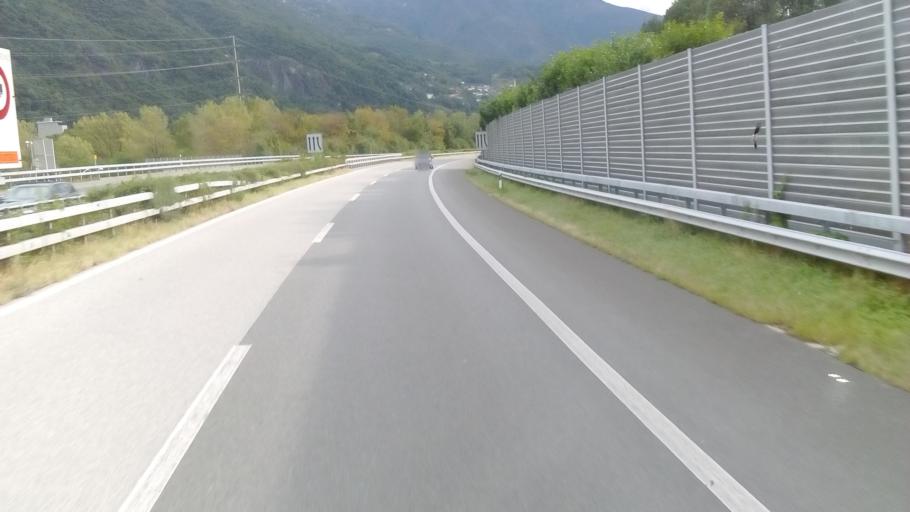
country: CH
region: Ticino
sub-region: Bellinzona District
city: Bellinzona
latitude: 46.2163
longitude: 9.0368
